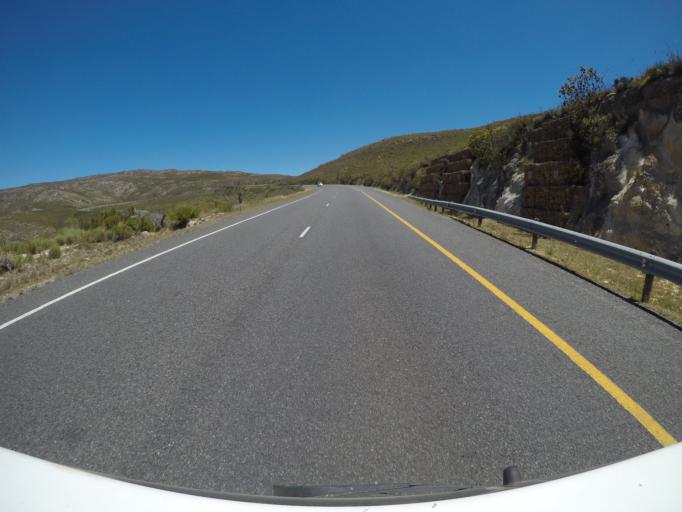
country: ZA
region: Western Cape
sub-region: Overberg District Municipality
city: Grabouw
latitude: -34.2216
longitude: 19.1799
